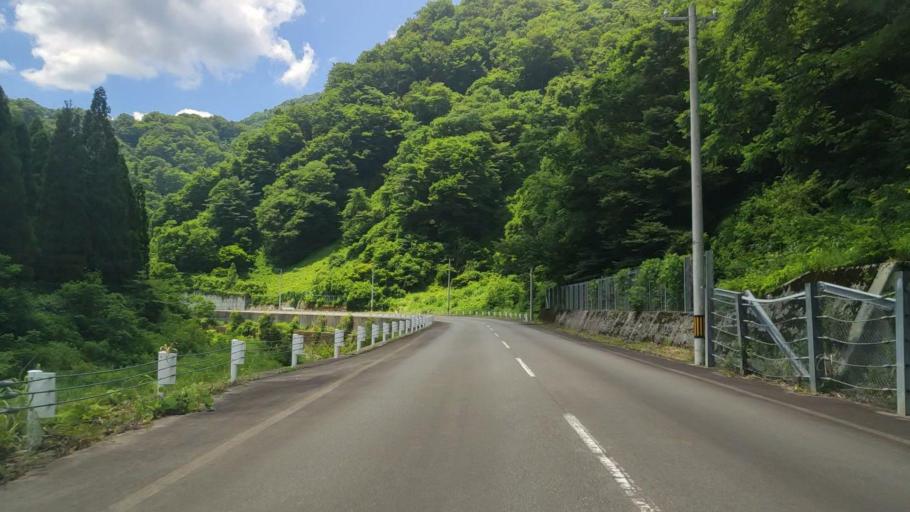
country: JP
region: Fukui
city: Ono
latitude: 35.8372
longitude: 136.4463
